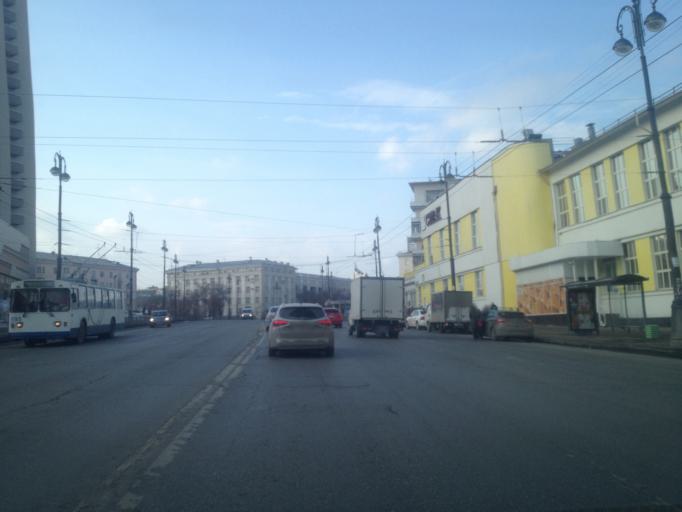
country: RU
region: Sverdlovsk
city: Yekaterinburg
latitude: 56.8487
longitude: 60.6081
